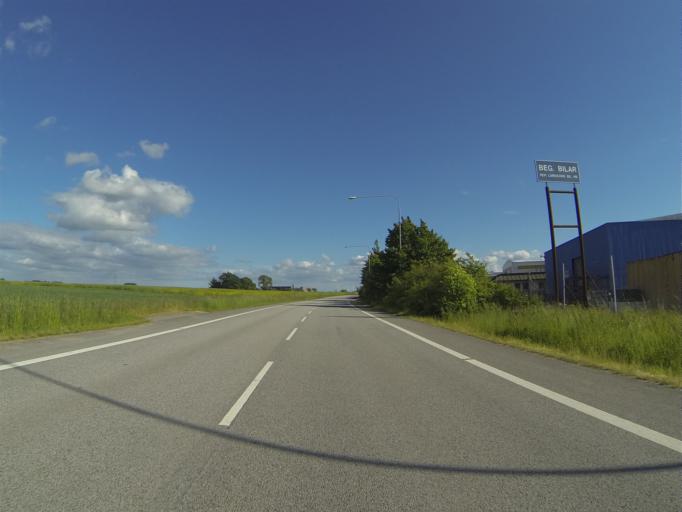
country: SE
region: Skane
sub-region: Staffanstorps Kommun
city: Staffanstorp
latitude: 55.6537
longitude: 13.2359
